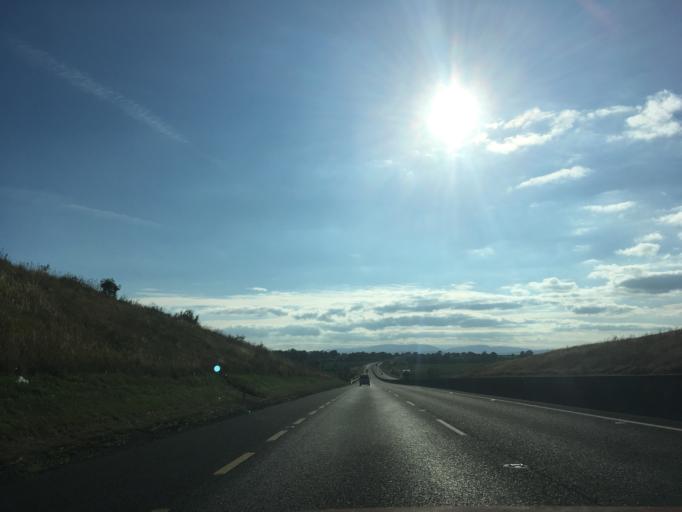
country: IE
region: Munster
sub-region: Waterford
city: Waterford
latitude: 52.2896
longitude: -7.0742
